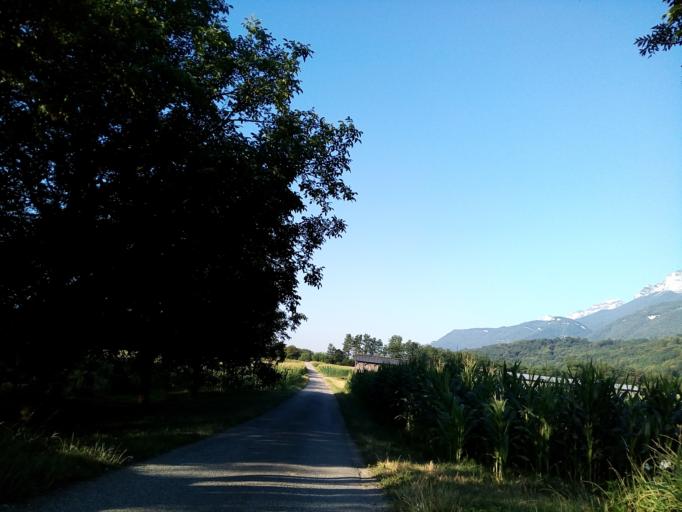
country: FR
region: Rhone-Alpes
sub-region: Departement de l'Isere
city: Barraux
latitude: 45.4054
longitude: 5.9857
